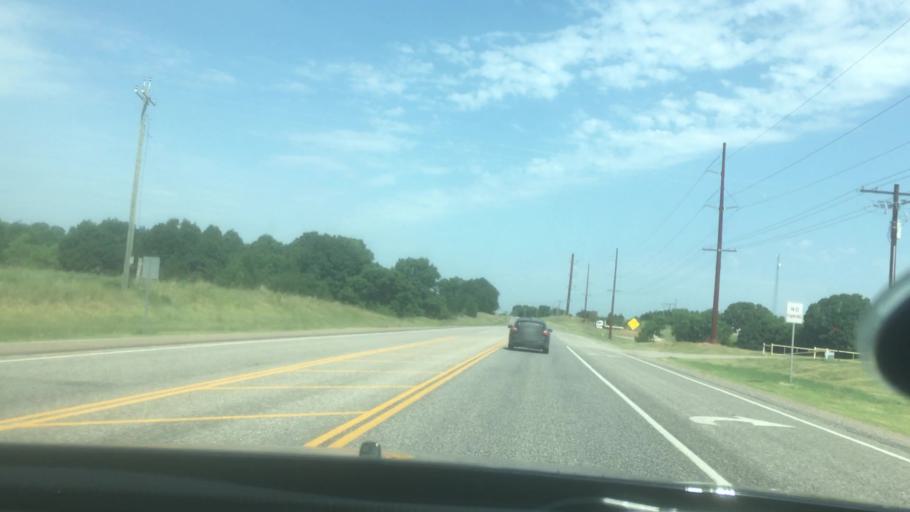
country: US
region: Oklahoma
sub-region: Seminole County
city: Konawa
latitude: 34.8649
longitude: -96.8300
